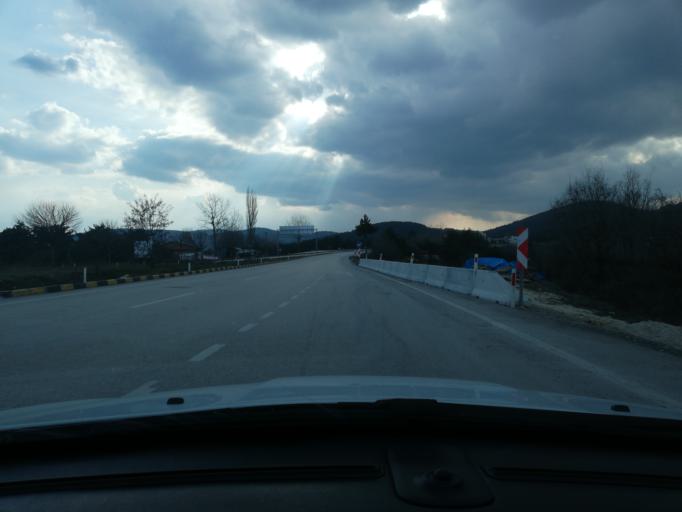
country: TR
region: Kastamonu
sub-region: Cide
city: Kastamonu
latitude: 41.3639
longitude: 33.7243
